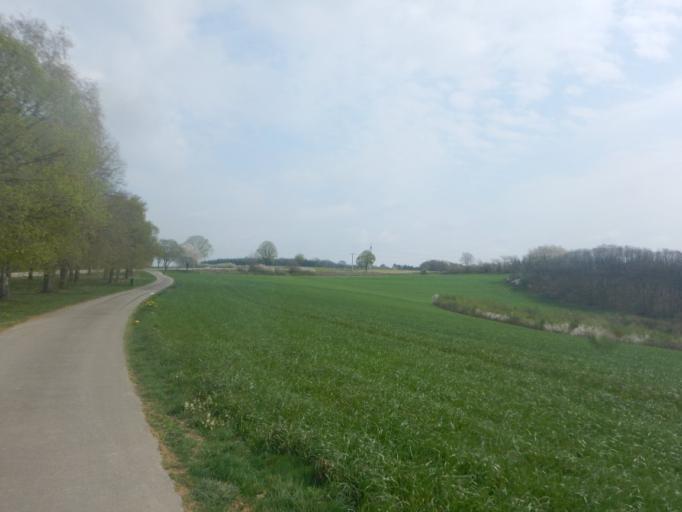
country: LU
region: Diekirch
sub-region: Canton de Wiltz
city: Esch-sur-Sure
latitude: 49.9200
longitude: 5.9182
